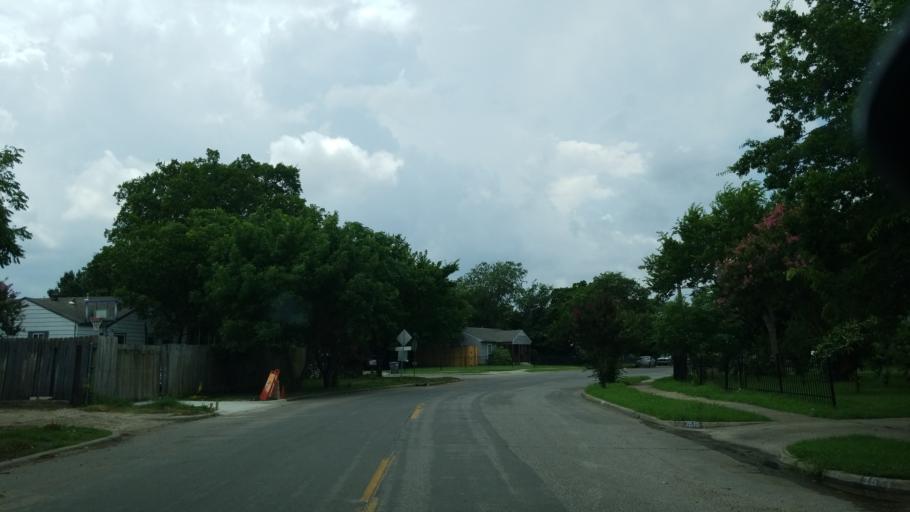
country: US
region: Texas
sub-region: Dallas County
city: Farmers Branch
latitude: 32.8750
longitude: -96.8599
